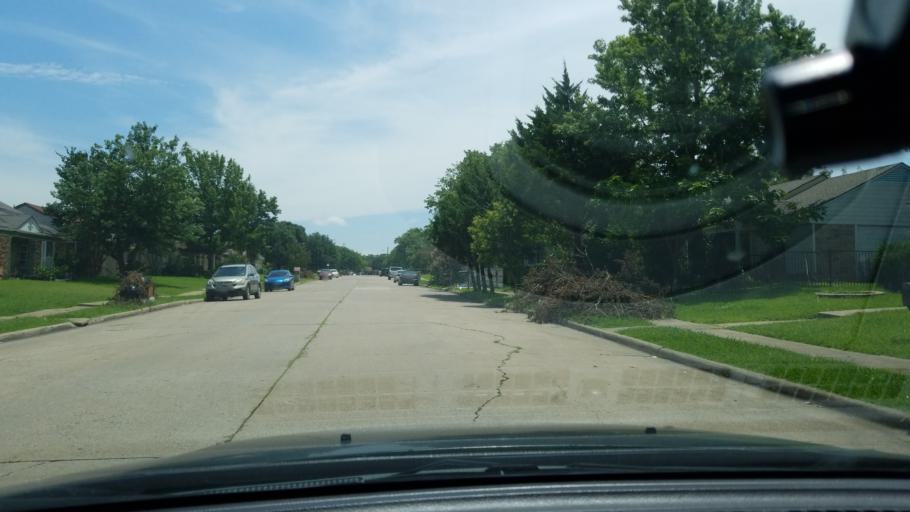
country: US
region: Texas
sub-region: Dallas County
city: Balch Springs
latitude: 32.7425
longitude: -96.6450
